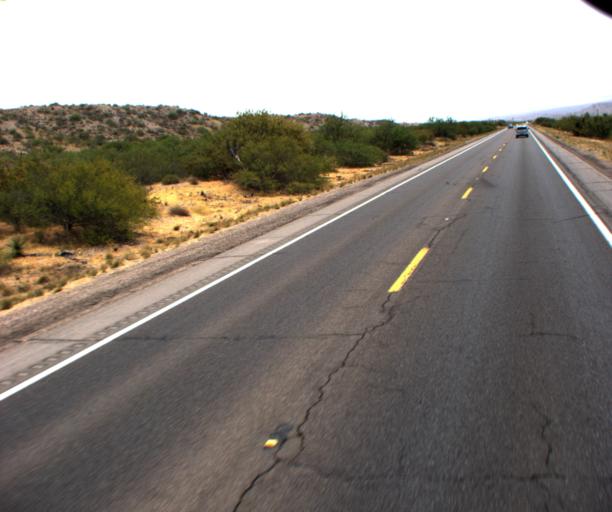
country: US
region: Arizona
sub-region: Gila County
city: Globe
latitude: 33.3700
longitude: -110.7276
